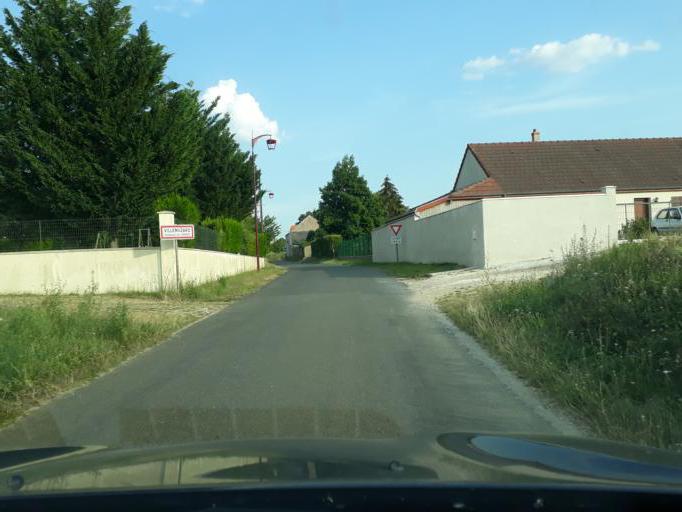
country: FR
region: Centre
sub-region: Departement du Loir-et-Cher
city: Mer
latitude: 47.8024
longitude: 1.4898
